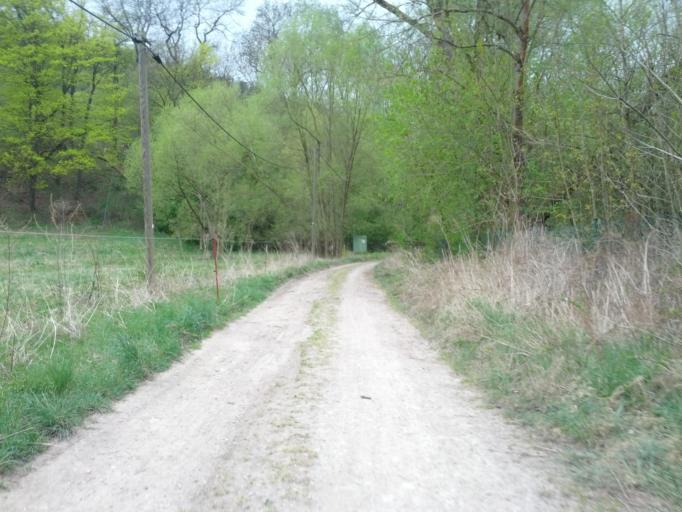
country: DE
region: Thuringia
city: Eisenach
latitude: 50.9631
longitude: 10.3602
